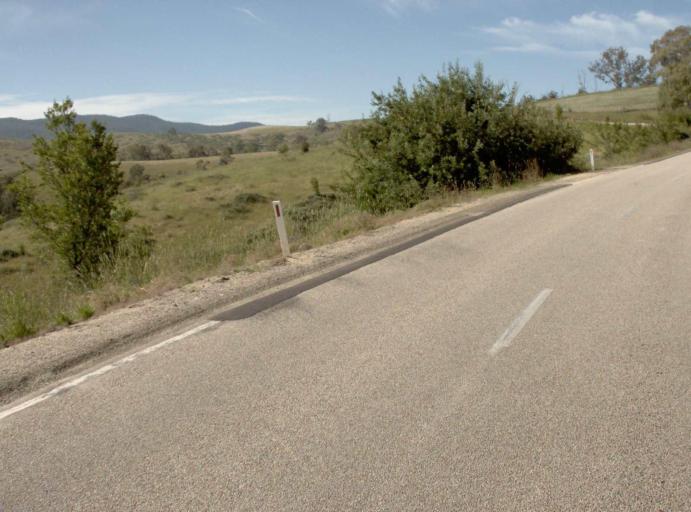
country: AU
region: Victoria
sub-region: East Gippsland
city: Lakes Entrance
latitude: -37.5074
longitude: 148.1711
